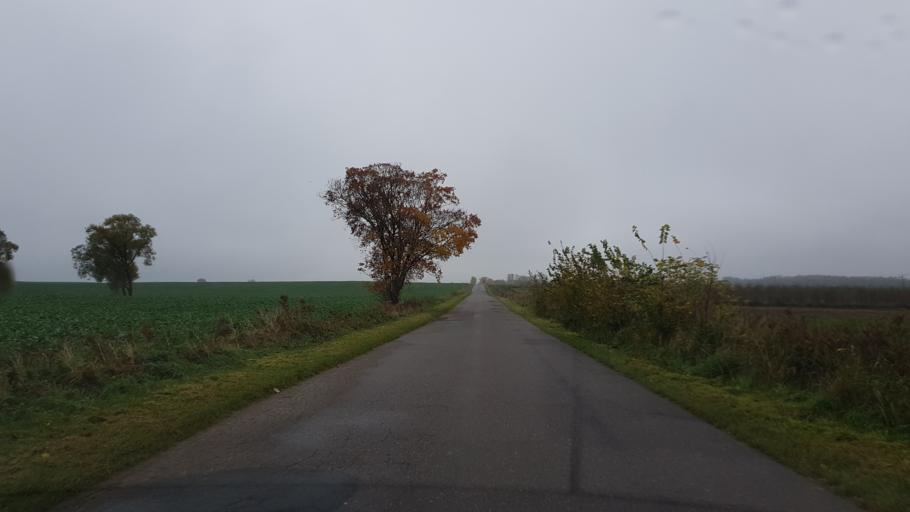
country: PL
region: West Pomeranian Voivodeship
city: Trzcinsko Zdroj
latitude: 53.0737
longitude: 14.5307
